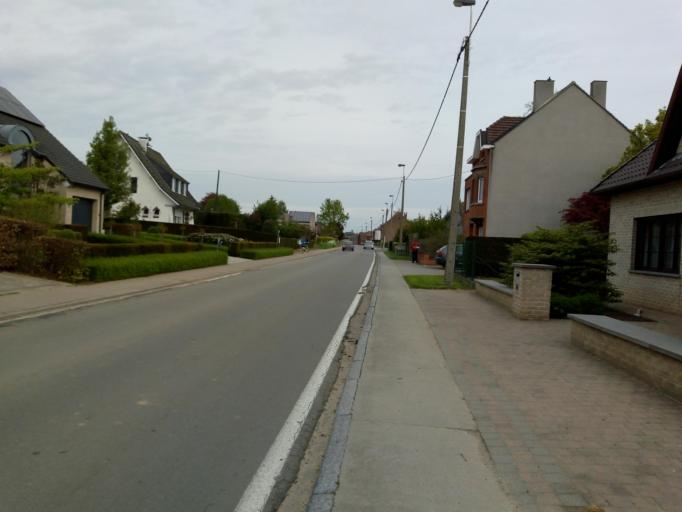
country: BE
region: Flanders
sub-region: Provincie Vlaams-Brabant
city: Sint-Martens-Lennik
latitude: 50.8169
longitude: 4.1670
